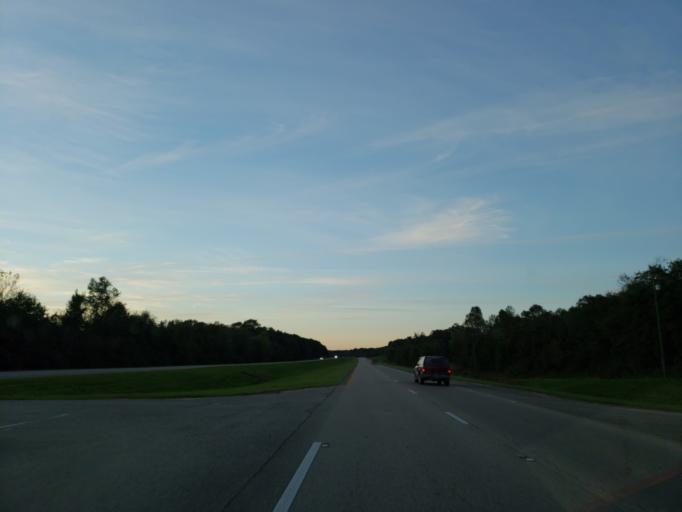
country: US
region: Mississippi
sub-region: Wayne County
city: Belmont
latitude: 31.5938
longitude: -88.5517
